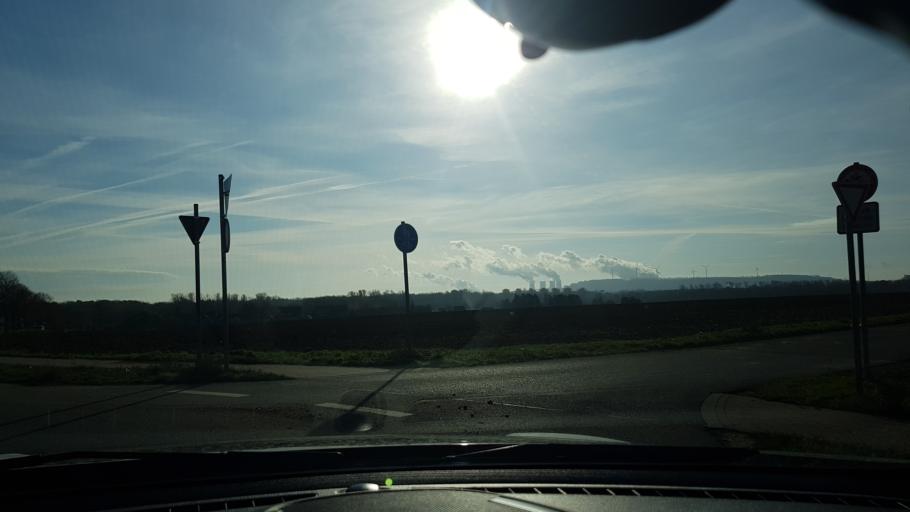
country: DE
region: North Rhine-Westphalia
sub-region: Regierungsbezirk Dusseldorf
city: Neubrueck
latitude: 51.1260
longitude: 6.6055
